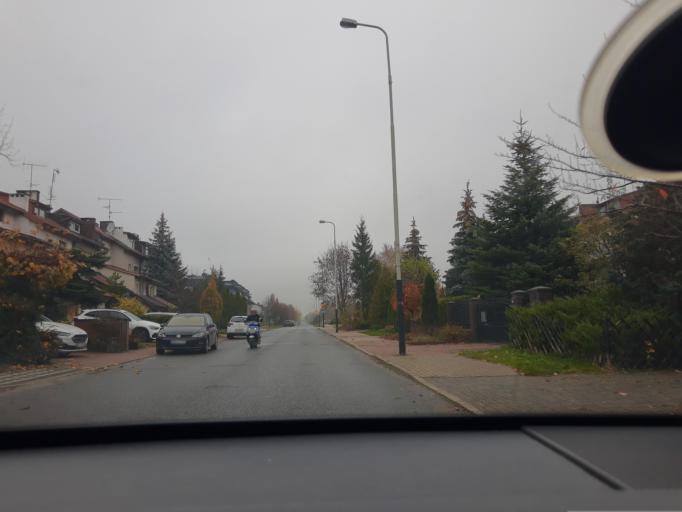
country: PL
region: Lodz Voivodeship
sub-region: Powiat pabianicki
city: Konstantynow Lodzki
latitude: 51.7407
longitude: 19.3791
